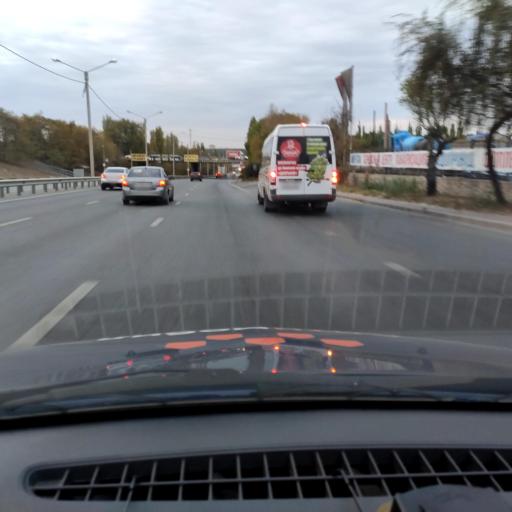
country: RU
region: Voronezj
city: Voronezh
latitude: 51.6600
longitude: 39.1321
